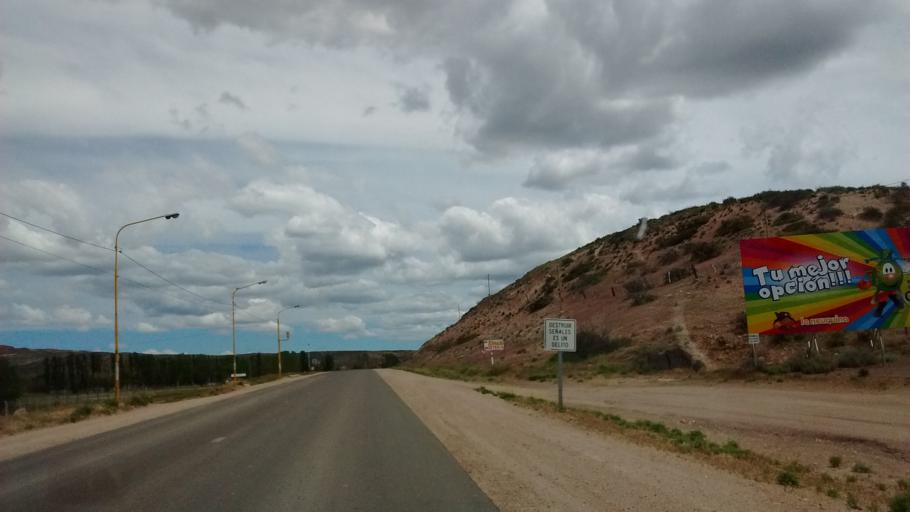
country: AR
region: Neuquen
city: Piedra del Aguila
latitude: -40.0534
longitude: -70.0825
